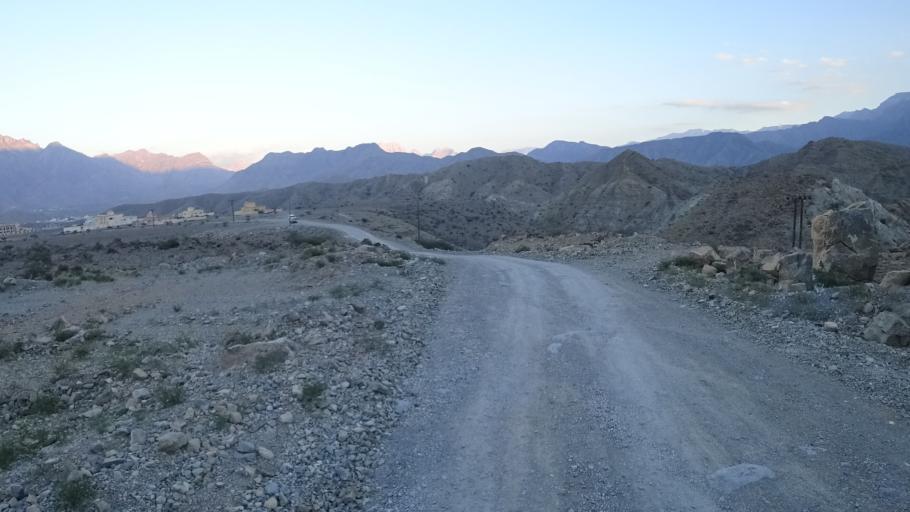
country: OM
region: Al Batinah
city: Rustaq
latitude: 23.2631
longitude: 57.3176
